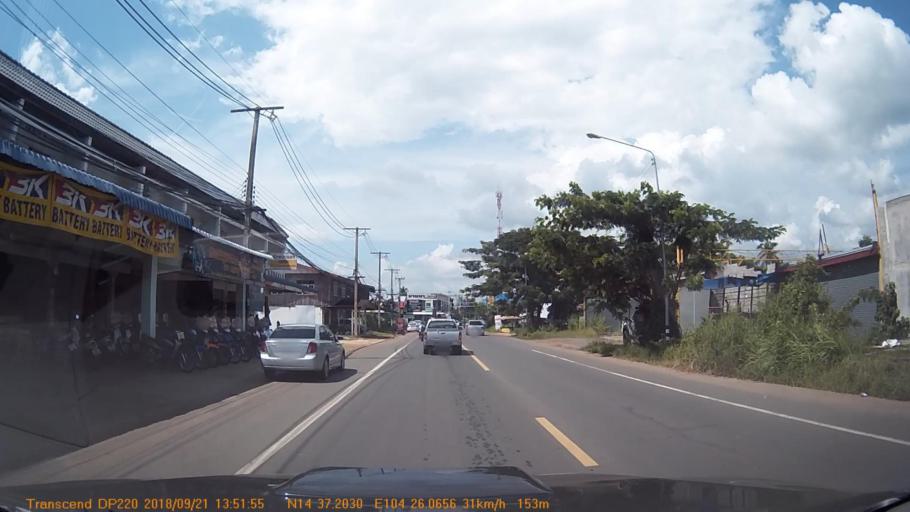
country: TH
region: Sisaket
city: Khun Han
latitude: 14.6202
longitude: 104.4344
